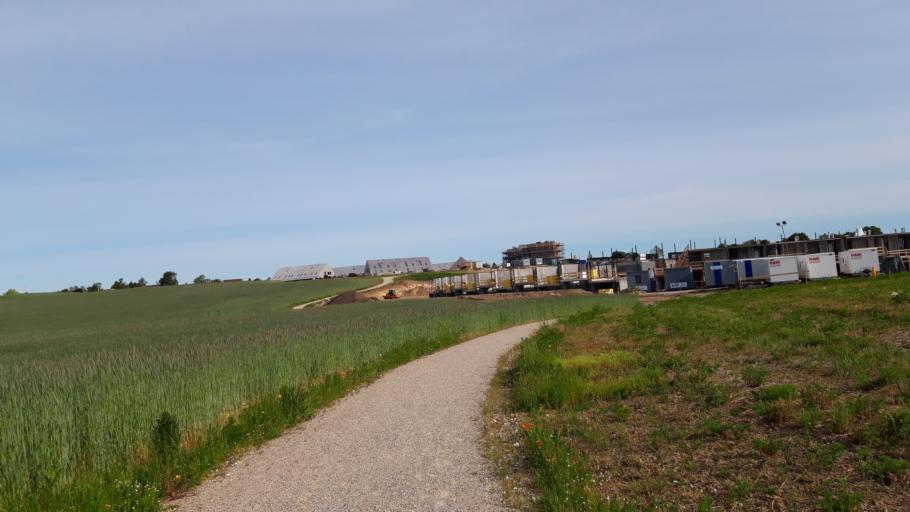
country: DK
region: Central Jutland
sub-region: Arhus Kommune
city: Lystrup
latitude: 56.2312
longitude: 10.2046
